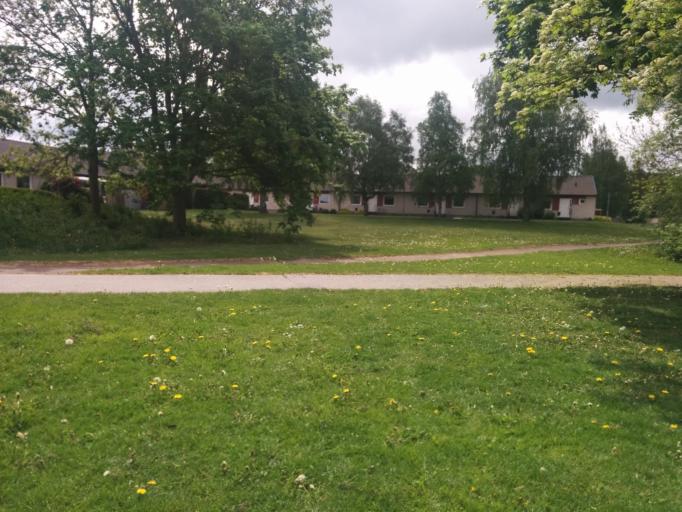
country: SE
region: Skane
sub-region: Lunds Kommun
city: Genarp
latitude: 55.5981
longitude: 13.3920
